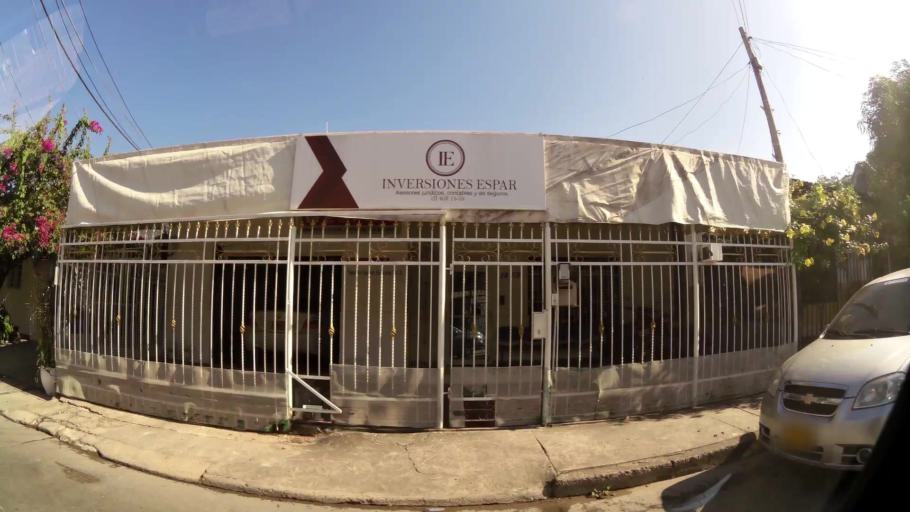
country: CO
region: Bolivar
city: Cartagena
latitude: 10.4294
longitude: -75.5369
